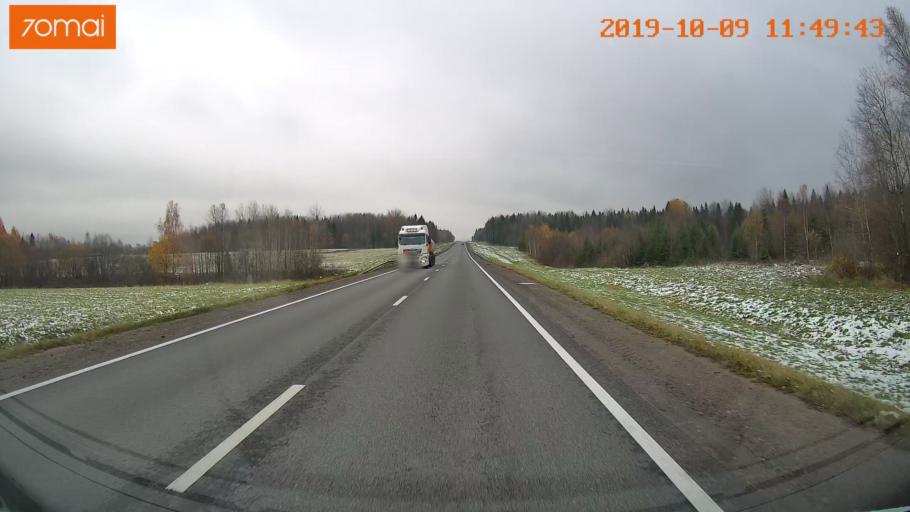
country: RU
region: Vologda
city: Gryazovets
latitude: 58.8150
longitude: 40.2345
